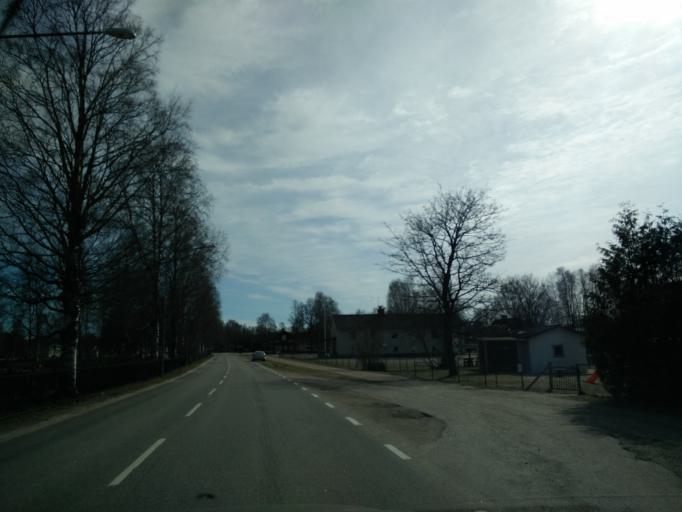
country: SE
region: Vaermland
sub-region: Hagfors Kommun
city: Hagfors
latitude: 60.0077
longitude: 13.5948
